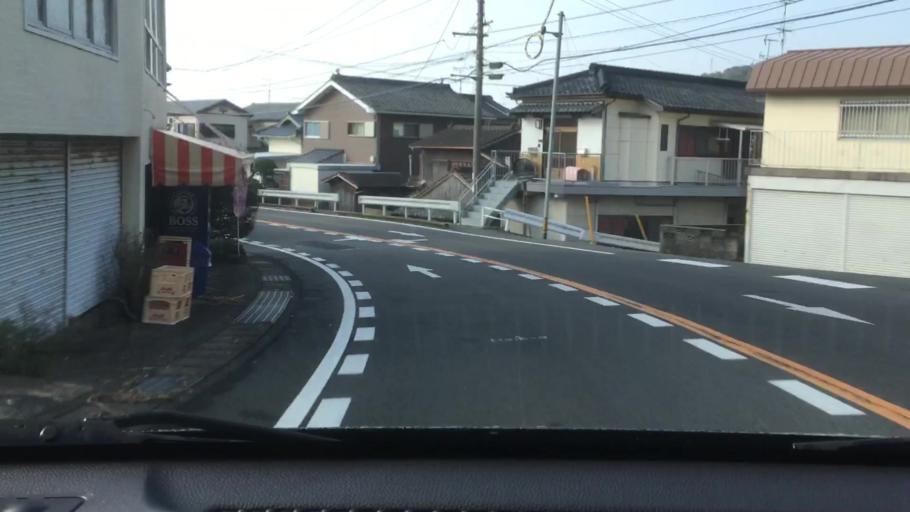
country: JP
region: Nagasaki
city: Togitsu
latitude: 32.9336
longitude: 129.6469
